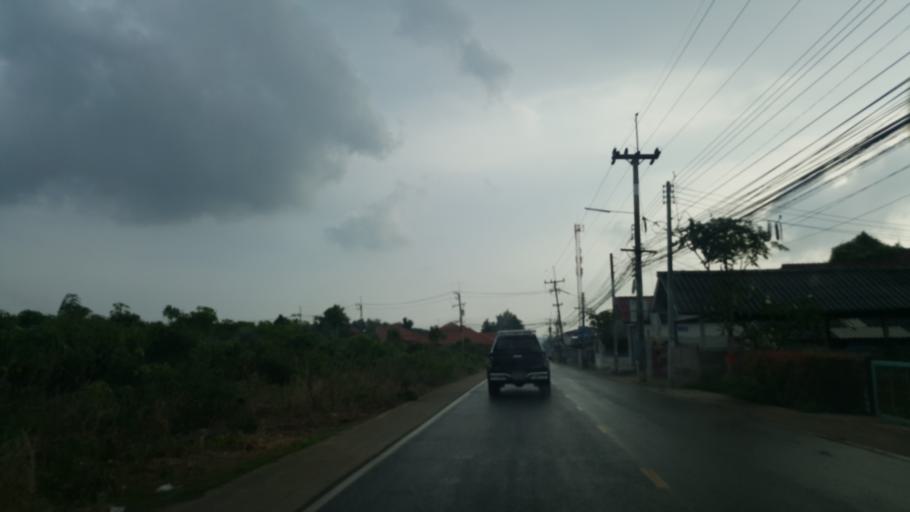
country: TH
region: Chon Buri
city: Sattahip
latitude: 12.6893
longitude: 100.9069
